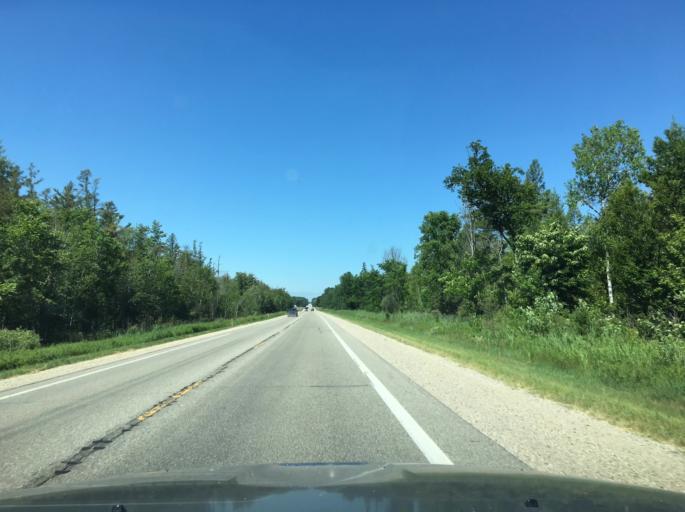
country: US
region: Michigan
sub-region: Osceola County
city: Reed City
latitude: 43.8728
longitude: -85.4076
